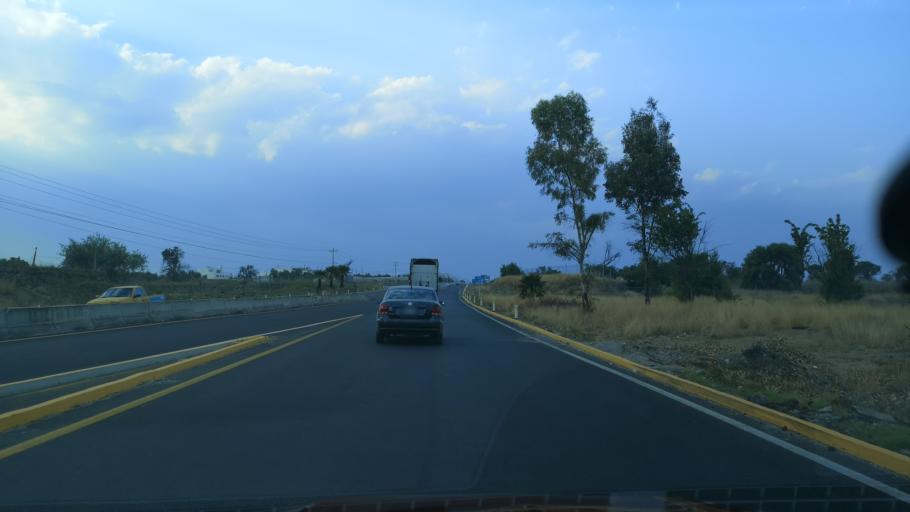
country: MX
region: Puebla
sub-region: Juan C. Bonilla
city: Santa Maria Zacatepec
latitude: 19.1349
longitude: -98.3735
